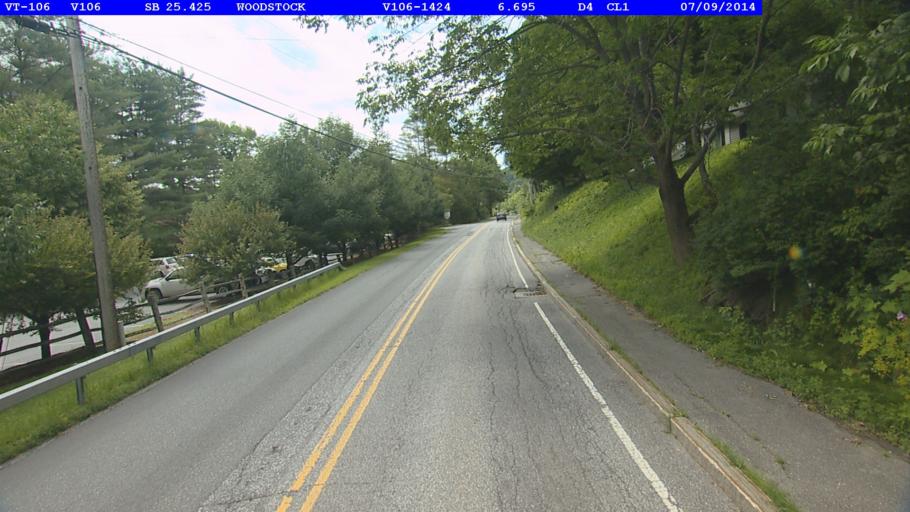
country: US
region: Vermont
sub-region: Windsor County
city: Woodstock
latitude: 43.6164
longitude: -72.5166
